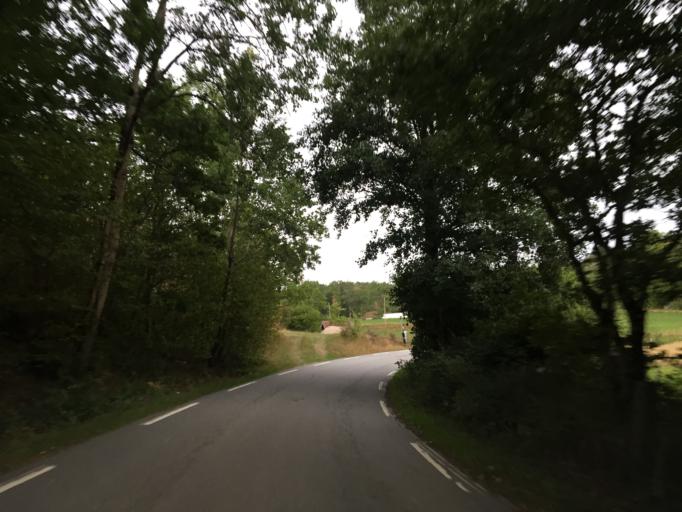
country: NO
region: Ostfold
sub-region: Hvaler
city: Skjaerhalden
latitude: 59.0528
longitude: 11.0044
